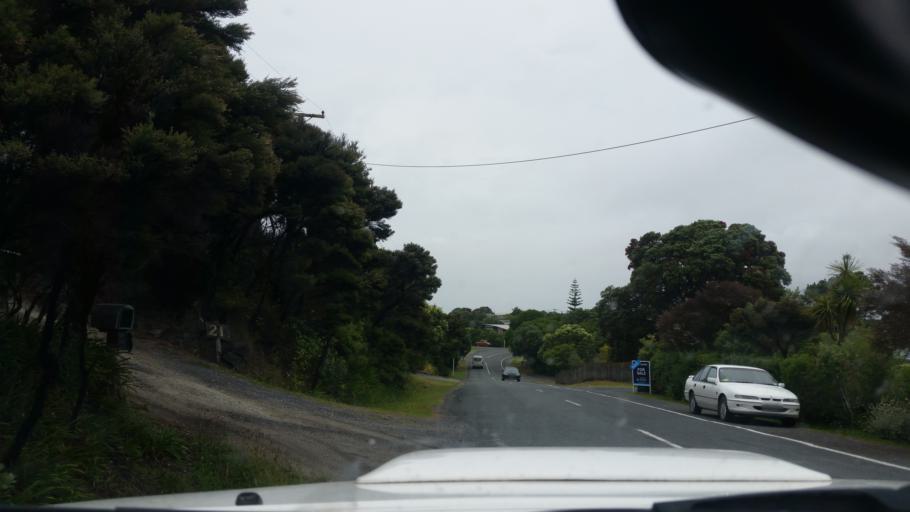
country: NZ
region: Auckland
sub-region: Auckland
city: Wellsford
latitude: -36.1016
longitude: 174.5890
